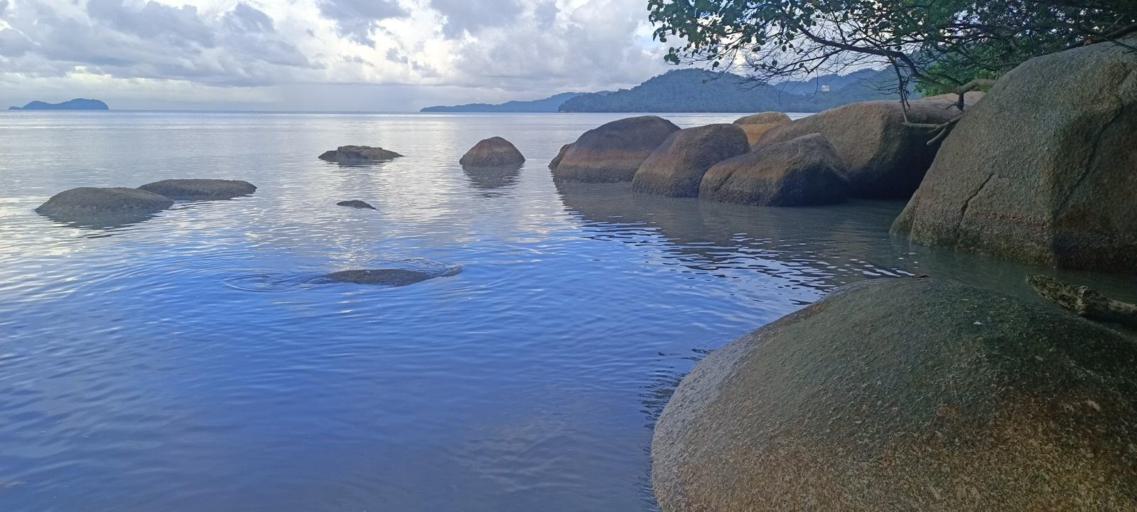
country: MY
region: Penang
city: Kampung Sungai Ara
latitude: 5.2705
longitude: 100.2688
